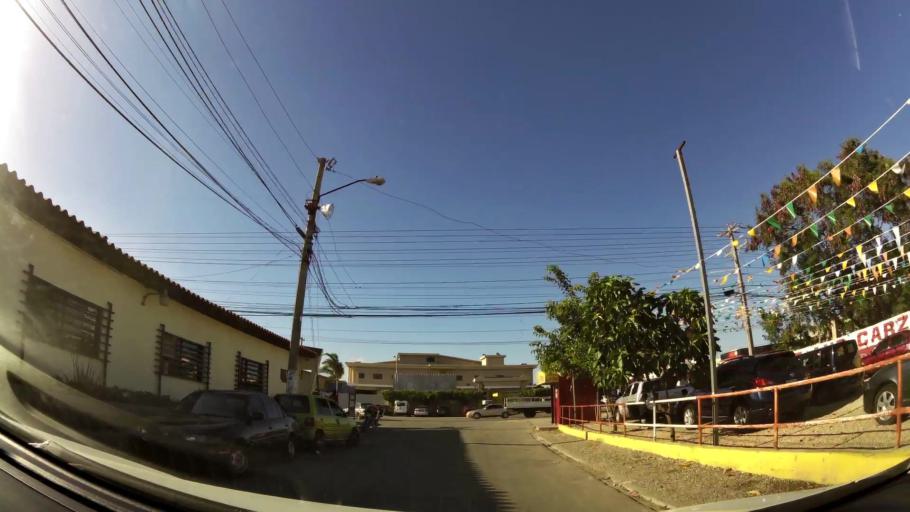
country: DO
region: Santo Domingo
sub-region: Santo Domingo
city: Santo Domingo Este
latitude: 18.4919
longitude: -69.8136
